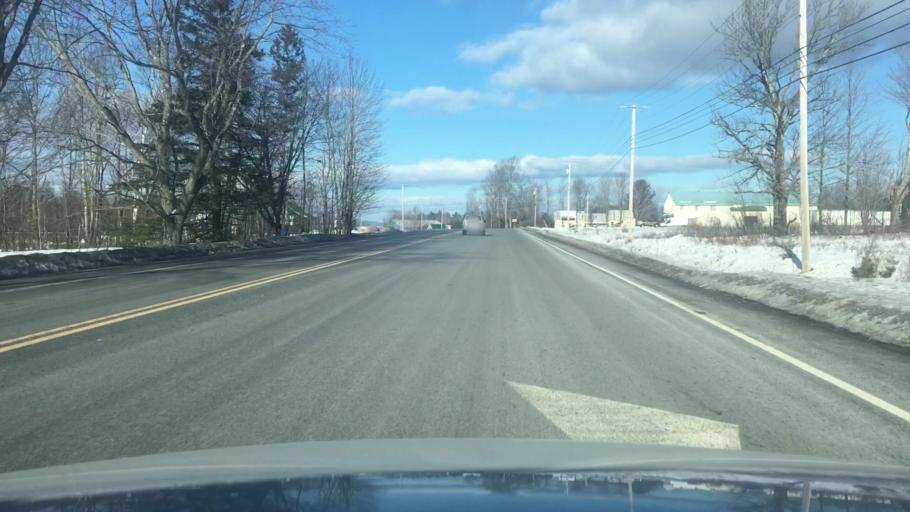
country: US
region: Maine
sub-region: Somerset County
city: Skowhegan
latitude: 44.8105
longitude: -69.7592
